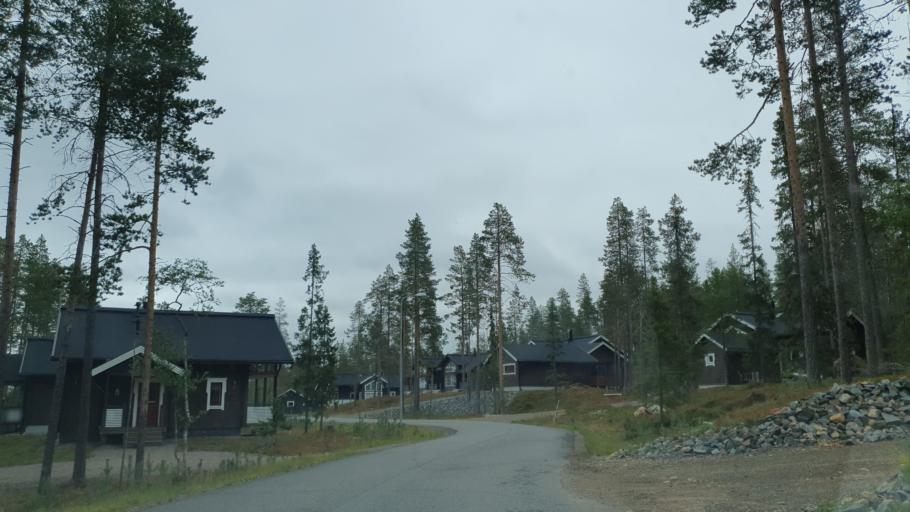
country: FI
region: Lapland
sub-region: Tunturi-Lappi
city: Kolari
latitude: 67.5925
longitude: 24.1761
